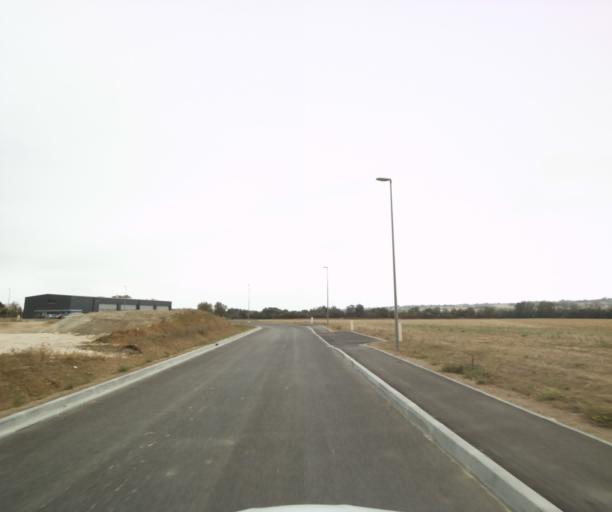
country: FR
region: Midi-Pyrenees
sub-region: Departement de la Haute-Garonne
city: Gardouch
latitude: 43.4067
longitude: 1.6962
